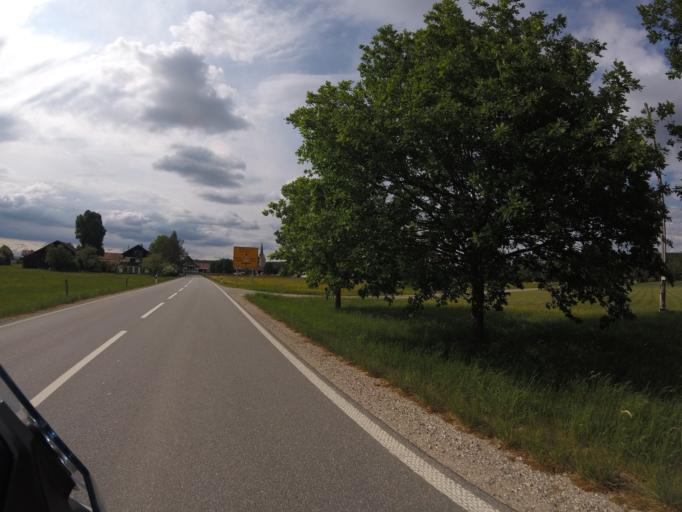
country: DE
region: Bavaria
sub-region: Upper Bavaria
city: Egling
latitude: 47.8864
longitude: 11.5066
